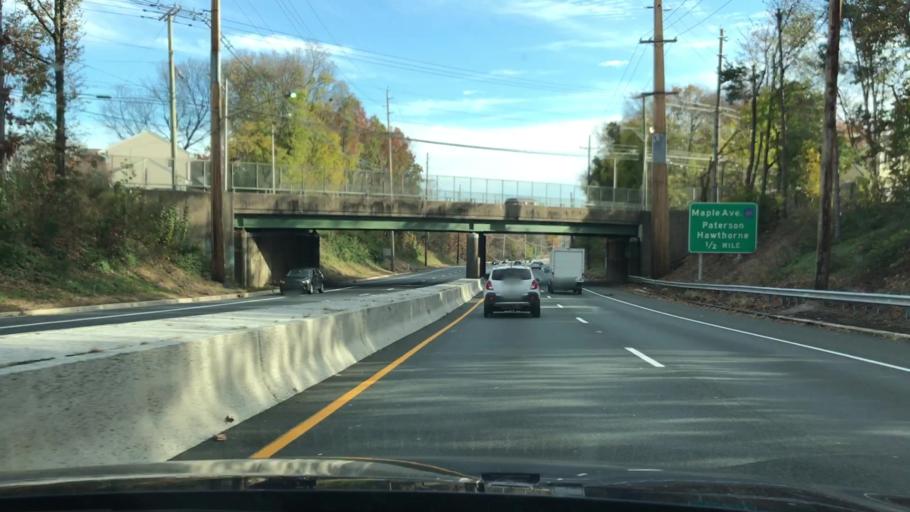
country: US
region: New Jersey
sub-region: Bergen County
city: Glen Rock
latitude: 40.9590
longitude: -74.1440
